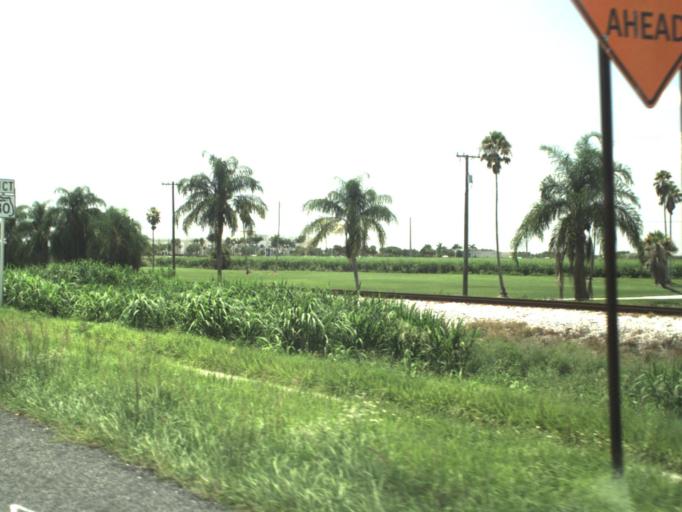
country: US
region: Florida
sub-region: Palm Beach County
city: Belle Glade
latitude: 26.7280
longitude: -80.6663
